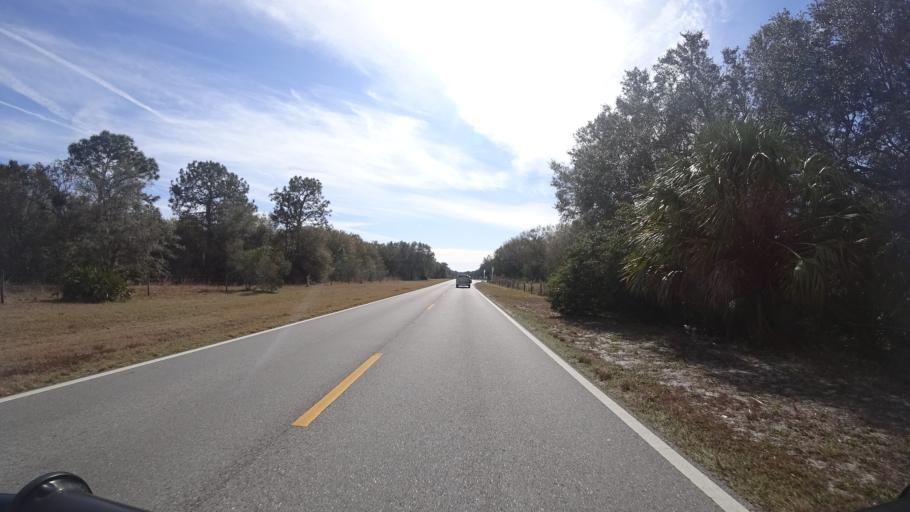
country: US
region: Florida
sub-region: Manatee County
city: Ellenton
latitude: 27.5273
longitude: -82.3681
